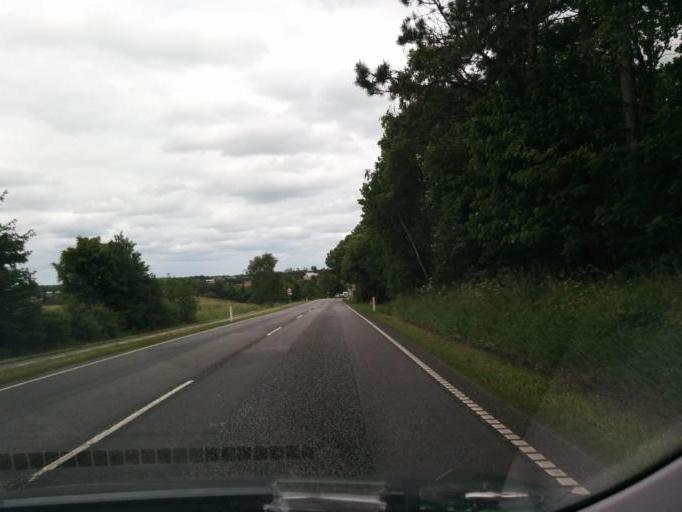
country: DK
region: Central Jutland
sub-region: Syddjurs Kommune
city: Ryomgard
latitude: 56.4384
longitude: 10.6681
